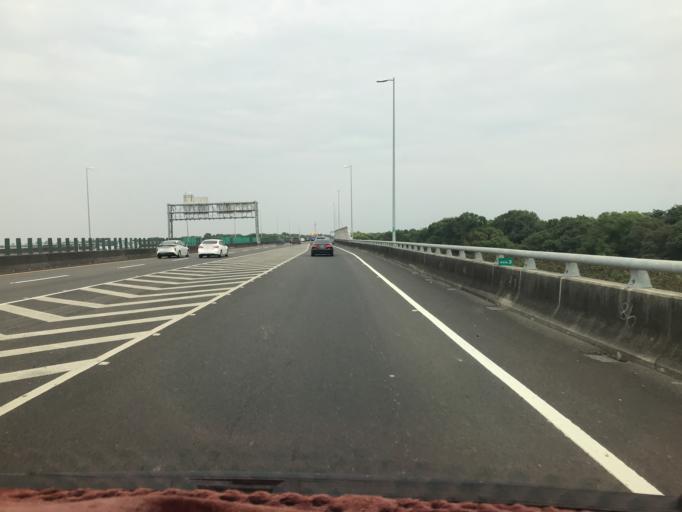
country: TW
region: Taiwan
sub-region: Pingtung
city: Pingtung
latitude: 22.6479
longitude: 120.5438
